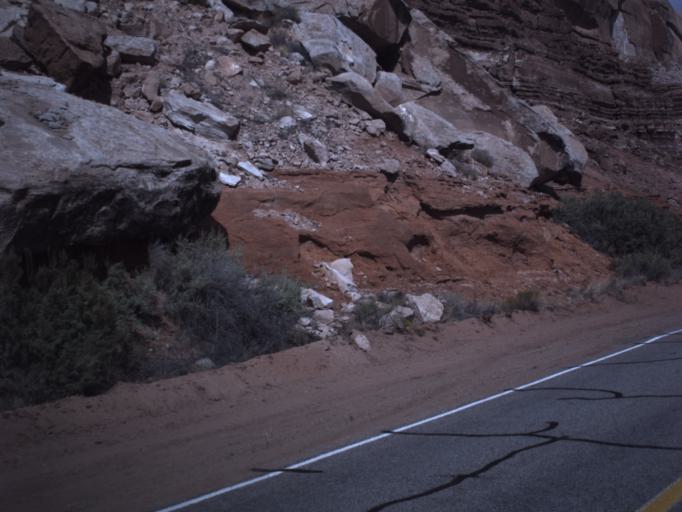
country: US
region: Utah
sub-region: San Juan County
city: Blanding
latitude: 37.2844
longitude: -109.5380
